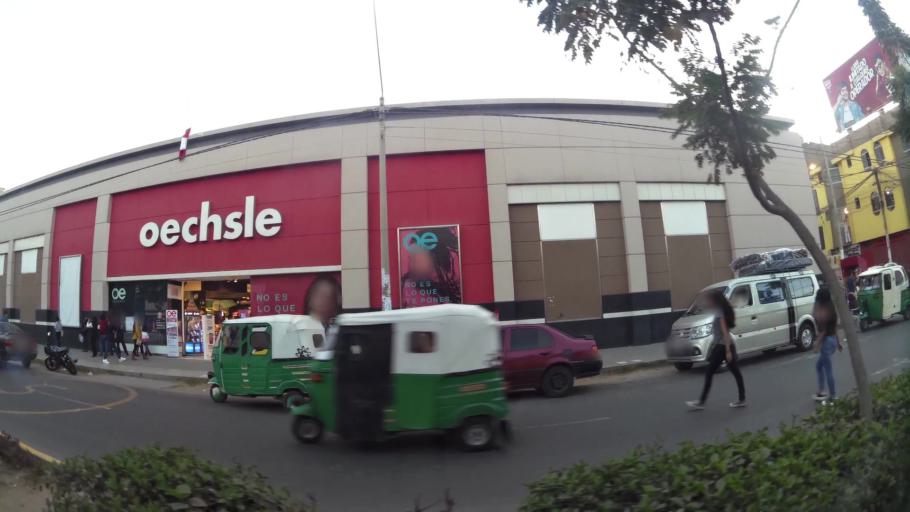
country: PE
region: Ica
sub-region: Provincia de Ica
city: Ica
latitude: -14.0651
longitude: -75.7305
